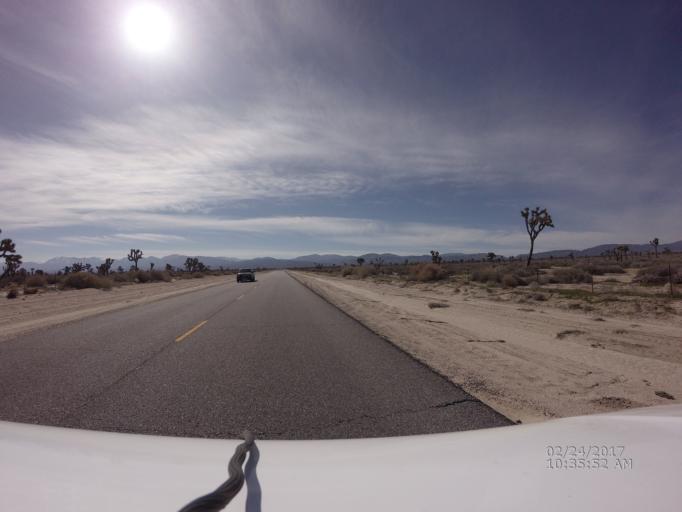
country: US
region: California
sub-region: Los Angeles County
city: Littlerock
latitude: 34.5996
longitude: -118.0051
